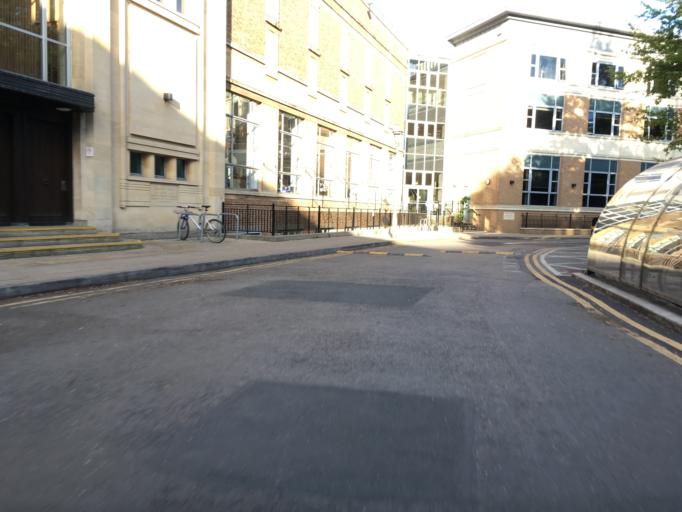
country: GB
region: England
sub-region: Bristol
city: Bristol
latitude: 51.4569
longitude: -2.6018
